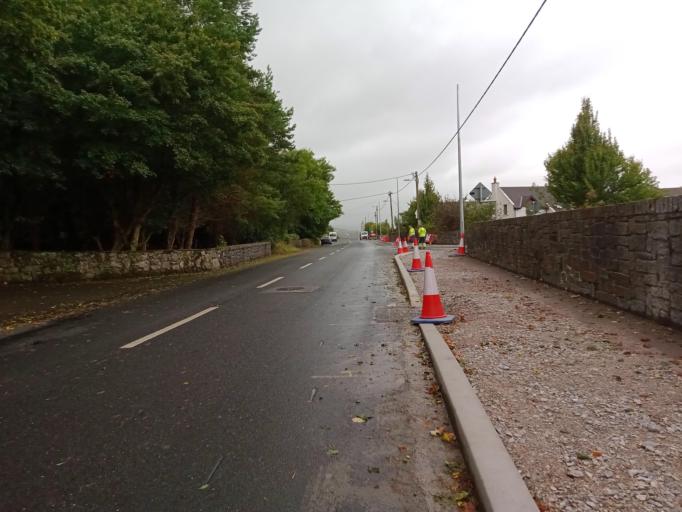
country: IE
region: Munster
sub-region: Waterford
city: Dungarvan
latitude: 52.0473
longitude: -7.5740
